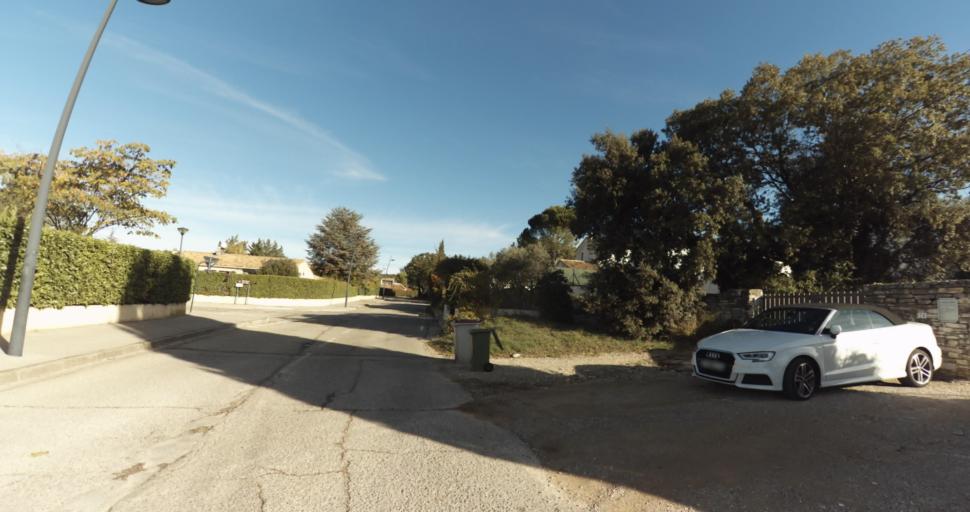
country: FR
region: Provence-Alpes-Cote d'Azur
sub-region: Departement des Bouches-du-Rhone
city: Venelles
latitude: 43.5916
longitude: 5.4720
